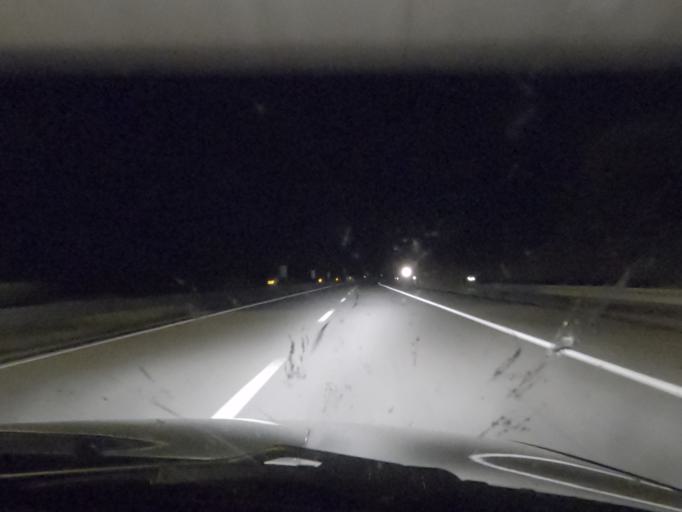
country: PT
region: Evora
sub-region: Estremoz
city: Estremoz
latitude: 38.8257
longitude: -7.6097
